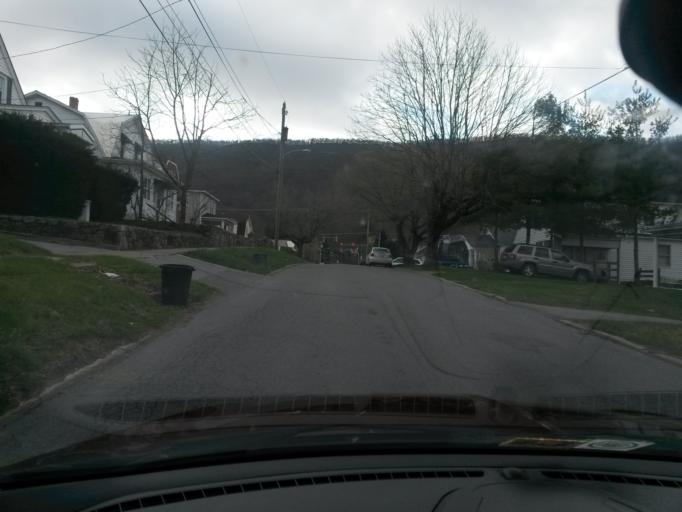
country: US
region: West Virginia
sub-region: Mercer County
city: Bluefield
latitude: 37.2515
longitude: -81.2149
